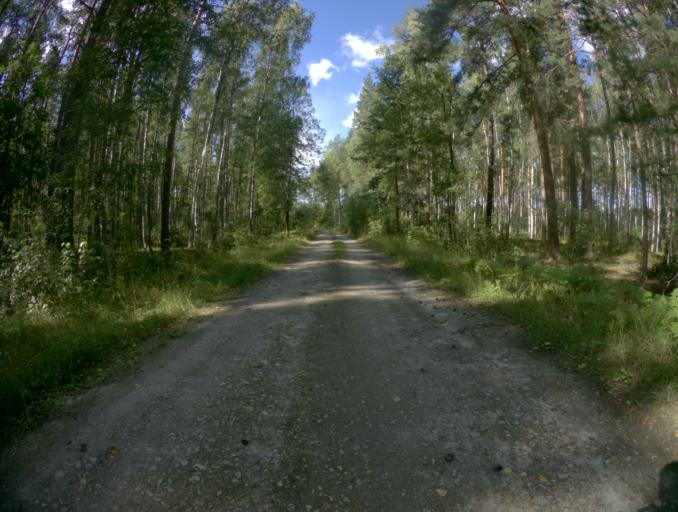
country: RU
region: Vladimir
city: Nikologory
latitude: 56.0195
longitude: 41.9191
